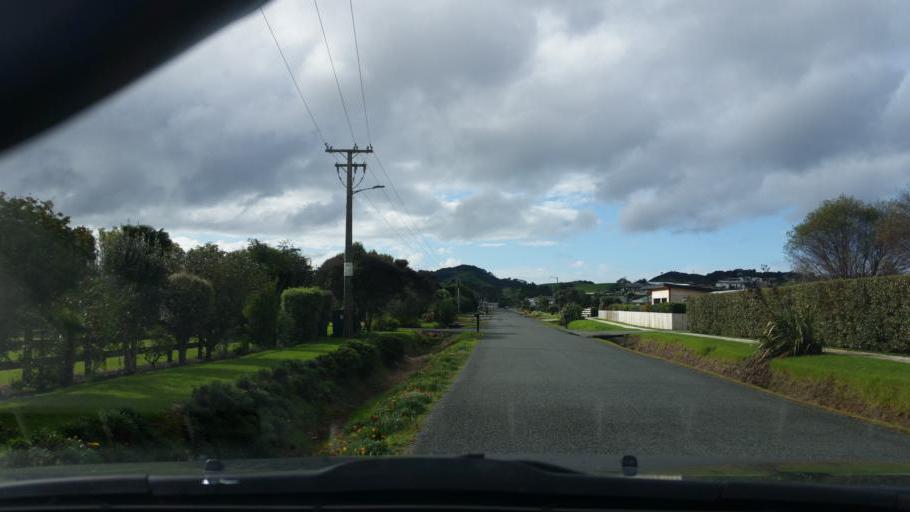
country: NZ
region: Auckland
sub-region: Auckland
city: Wellsford
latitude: -36.0904
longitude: 174.5733
